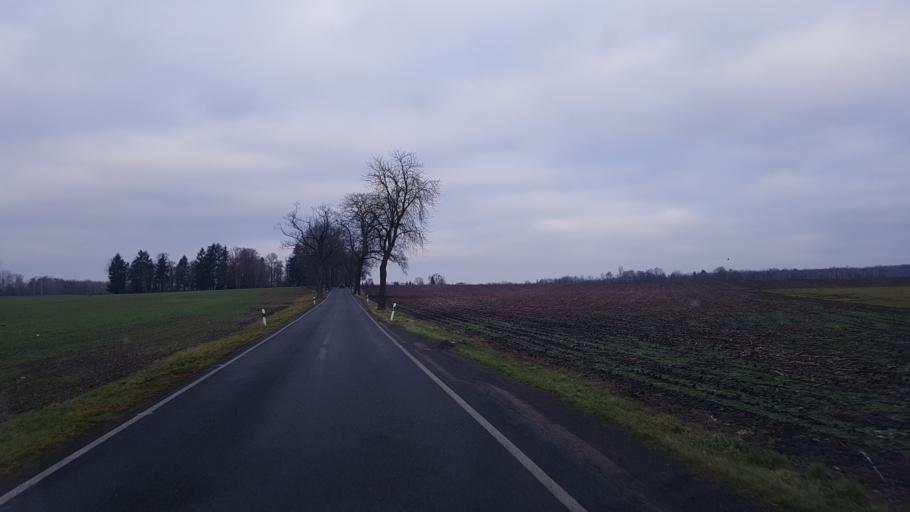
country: DE
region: Brandenburg
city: Schipkau
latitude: 51.5462
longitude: 13.8964
